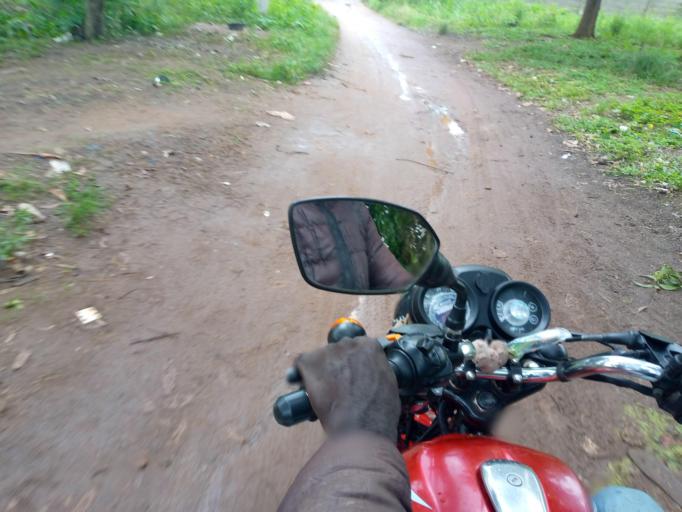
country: SL
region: Eastern Province
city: Kenema
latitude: 7.8472
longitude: -11.2051
